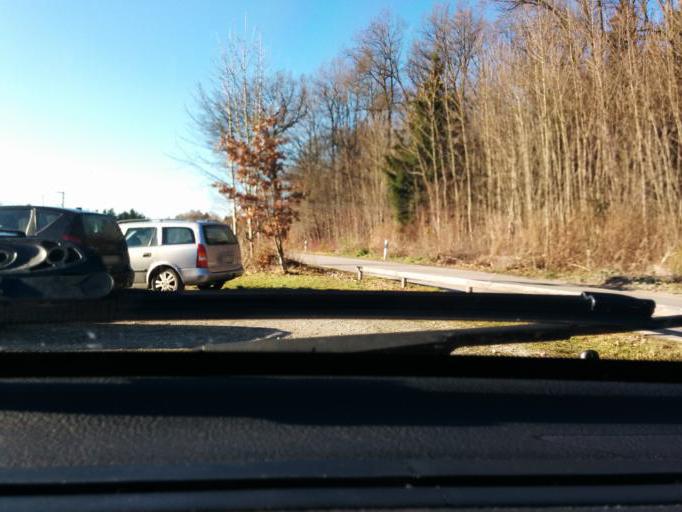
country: DE
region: Bavaria
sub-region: Upper Bavaria
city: Germering
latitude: 48.1608
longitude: 11.3947
